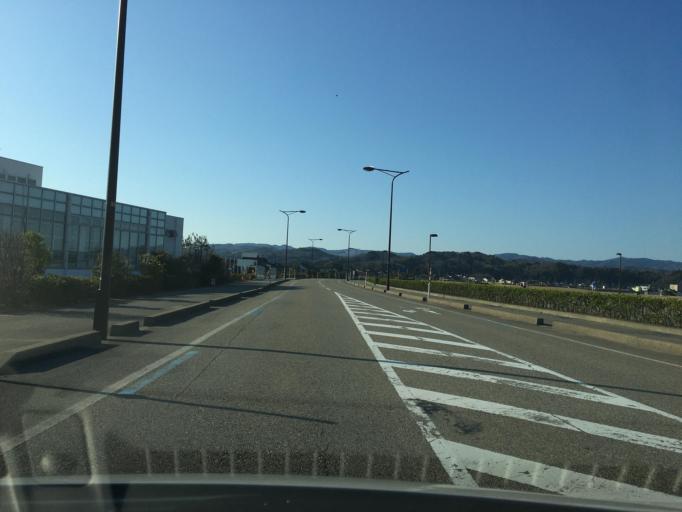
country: JP
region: Toyama
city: Himi
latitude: 36.8662
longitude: 136.9864
